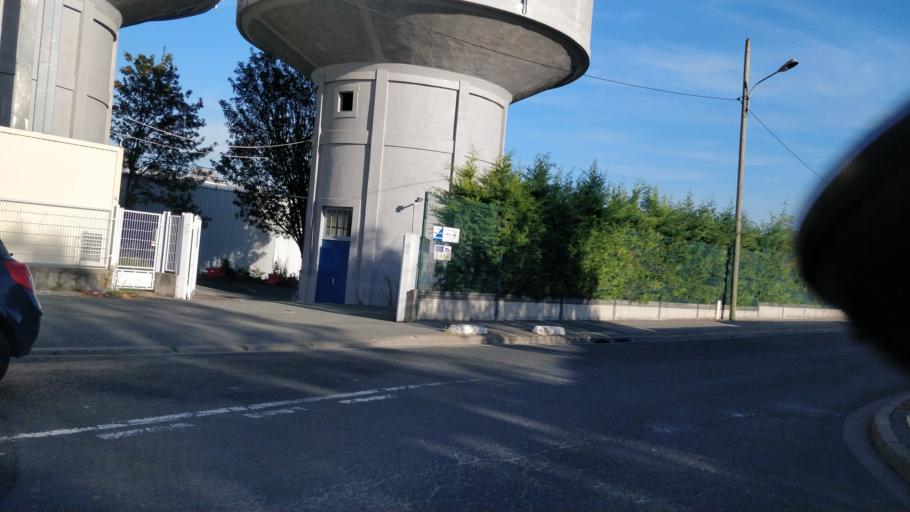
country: FR
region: Ile-de-France
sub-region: Departement des Hauts-de-Seine
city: Chatillon
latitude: 48.8039
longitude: 2.2980
